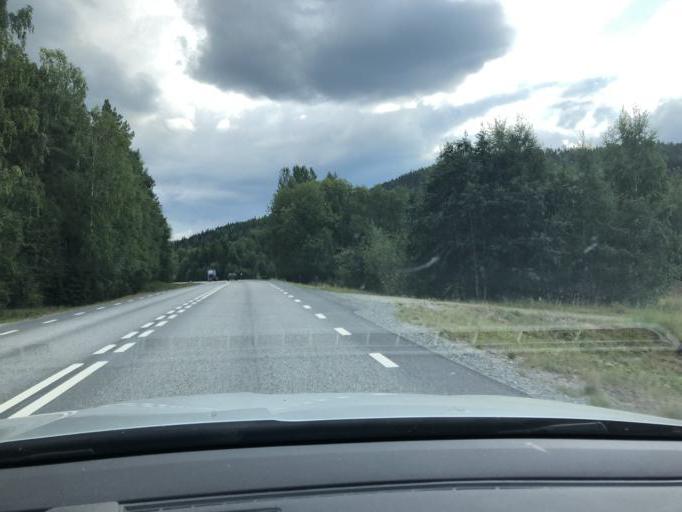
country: SE
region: Vaesternorrland
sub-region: Solleftea Kommun
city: Solleftea
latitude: 63.3091
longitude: 17.2003
